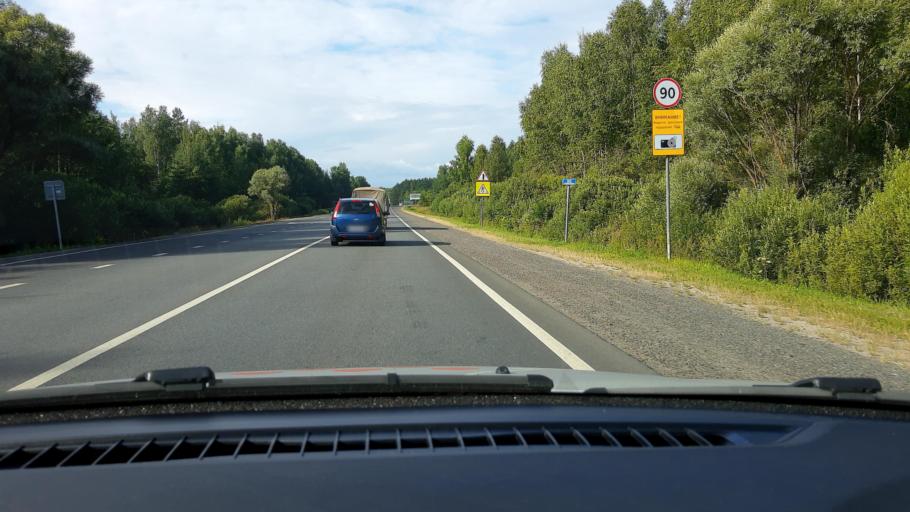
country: RU
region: Nizjnij Novgorod
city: Arzamas
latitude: 55.5180
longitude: 43.9061
